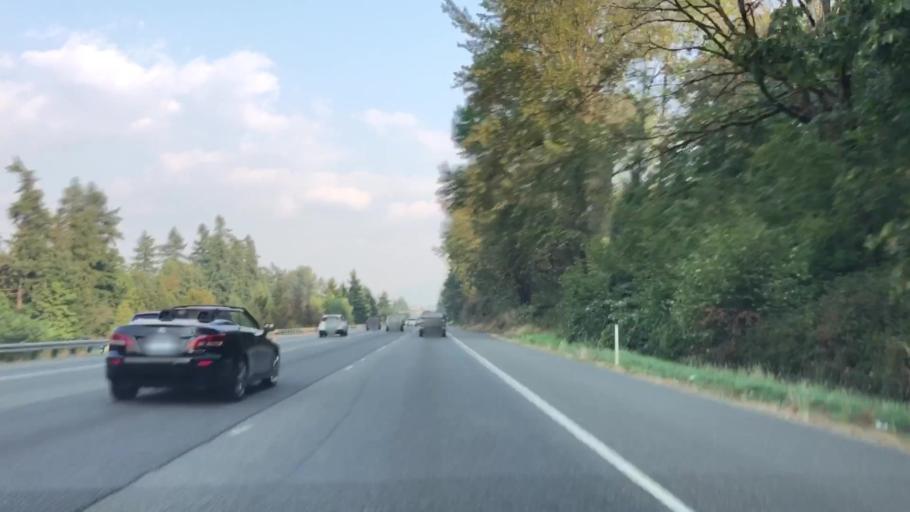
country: US
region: Washington
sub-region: King County
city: West Lake Sammamish
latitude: 47.5722
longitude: -122.1163
